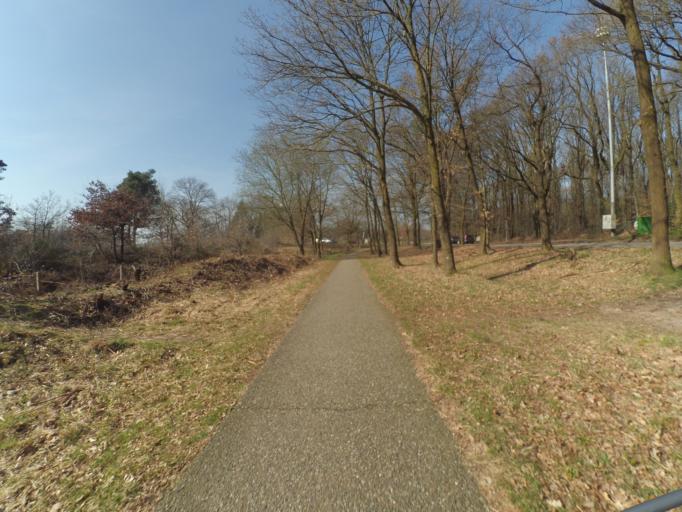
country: NL
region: Gelderland
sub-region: Gemeente Groesbeek
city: Groesbeek
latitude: 51.7824
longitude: 5.8884
